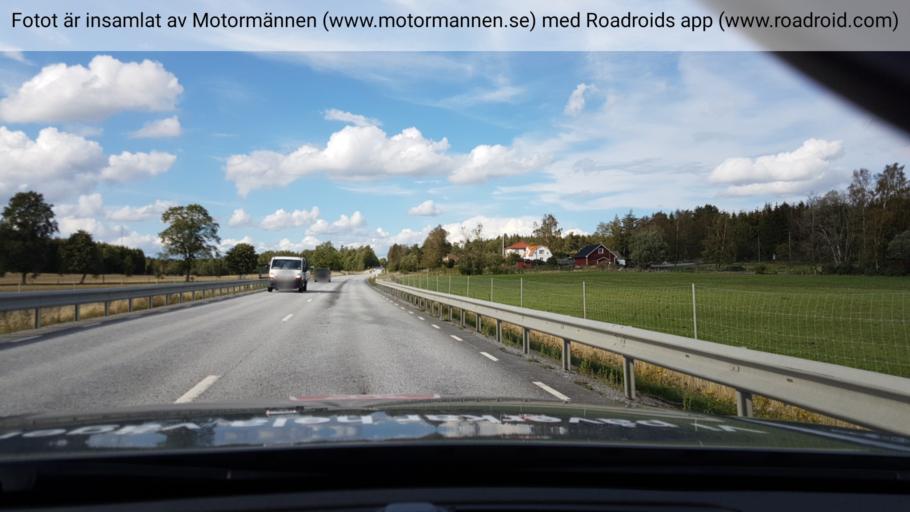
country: SE
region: Stockholm
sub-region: Upplands-Bro Kommun
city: Bro
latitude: 59.5995
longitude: 17.6117
